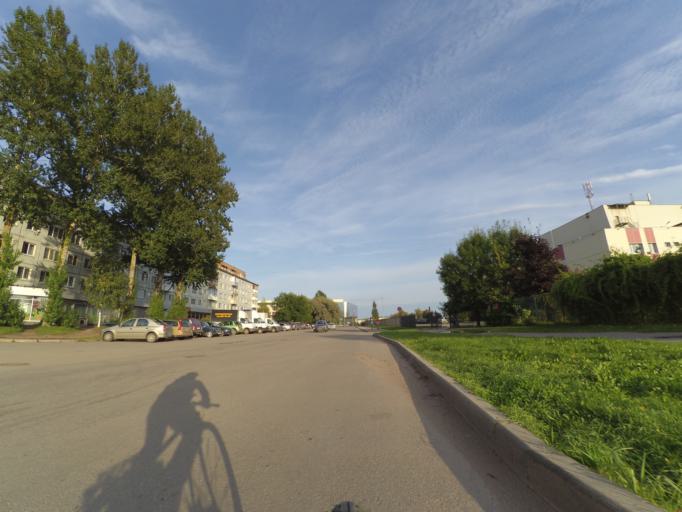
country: RU
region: Novgorod
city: Velikiy Novgorod
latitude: 58.5313
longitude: 31.2371
